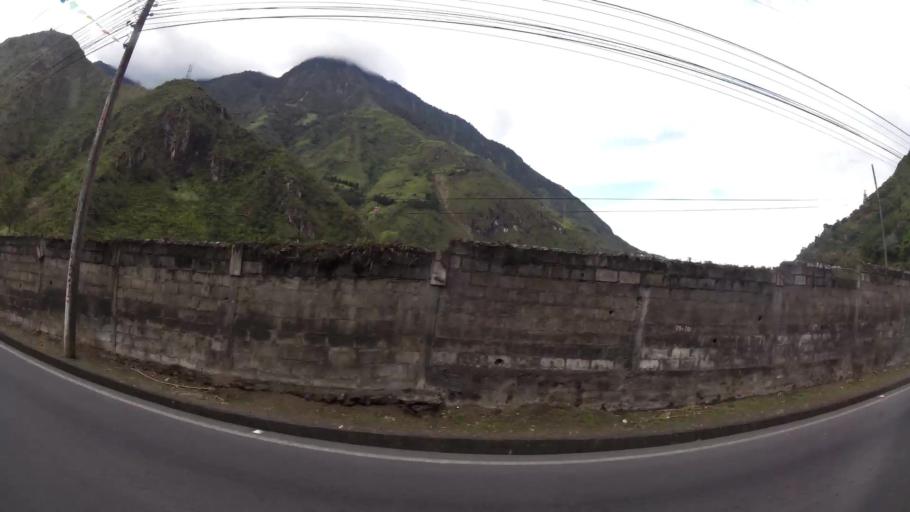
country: EC
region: Tungurahua
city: Banos
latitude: -1.3989
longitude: -78.3853
